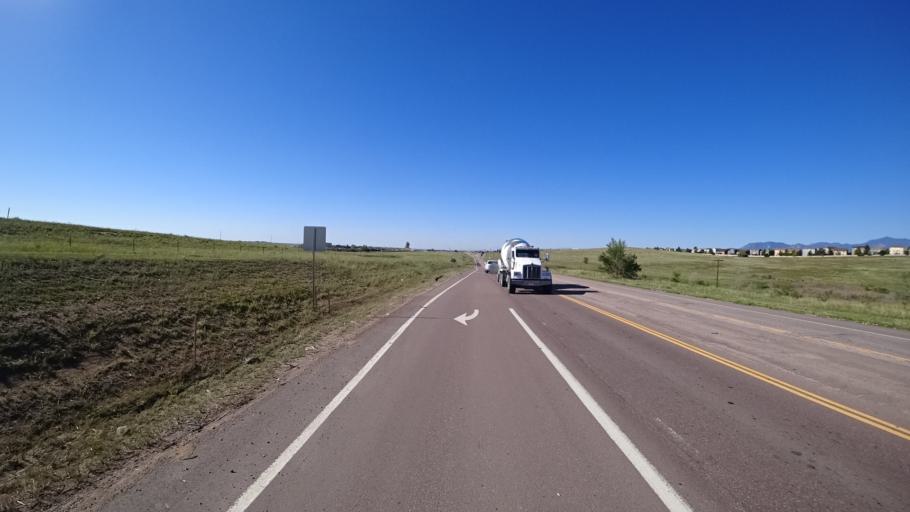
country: US
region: Colorado
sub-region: El Paso County
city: Cimarron Hills
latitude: 38.8934
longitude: -104.6827
